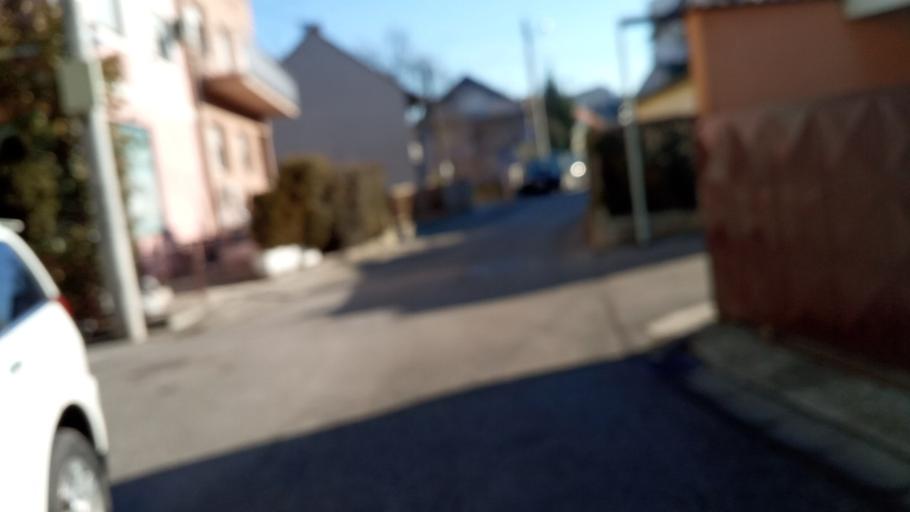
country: HR
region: Grad Zagreb
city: Jankomir
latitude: 45.7934
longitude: 15.9336
